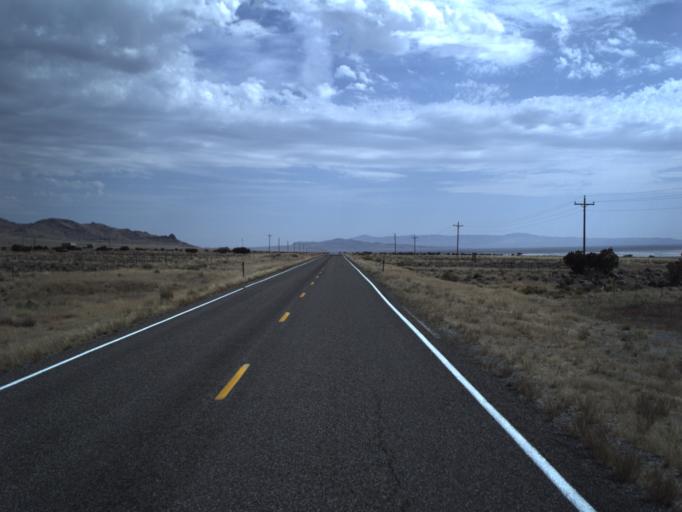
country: US
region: Utah
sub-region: Tooele County
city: Wendover
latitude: 41.4363
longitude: -113.7476
